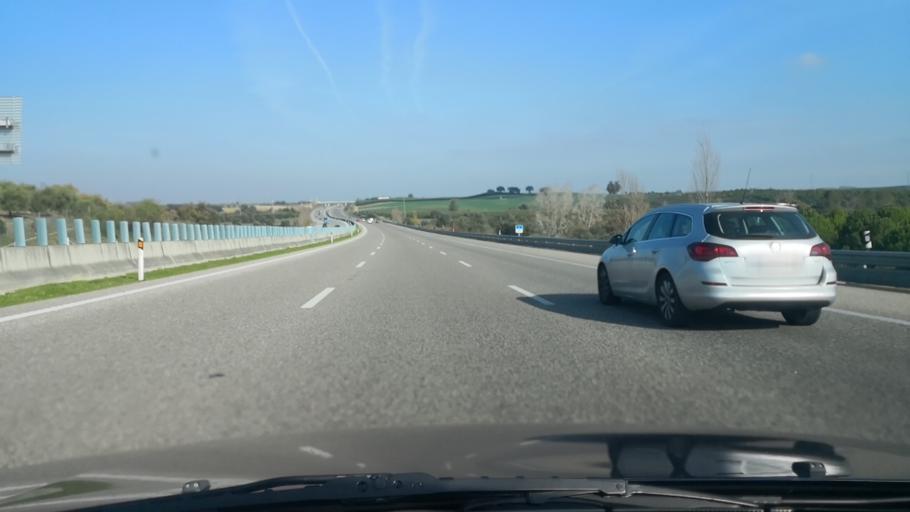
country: PT
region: Santarem
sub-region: Santarem
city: Santarem
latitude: 39.3165
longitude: -8.6671
